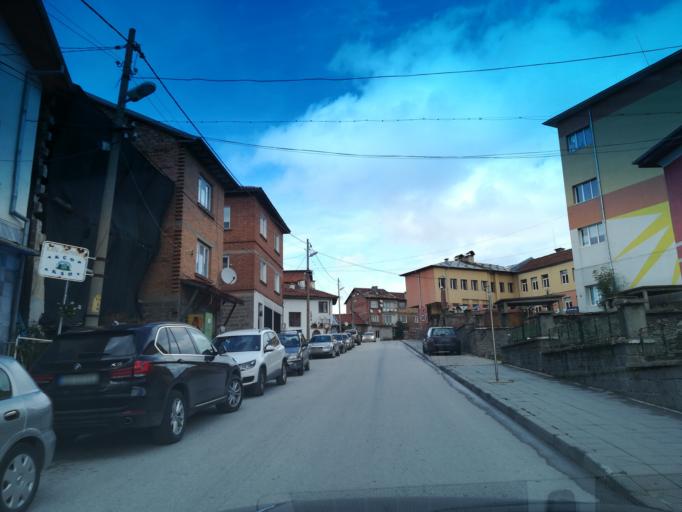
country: BG
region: Pazardzhik
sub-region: Obshtina Batak
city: Batak
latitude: 41.9374
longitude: 24.2707
